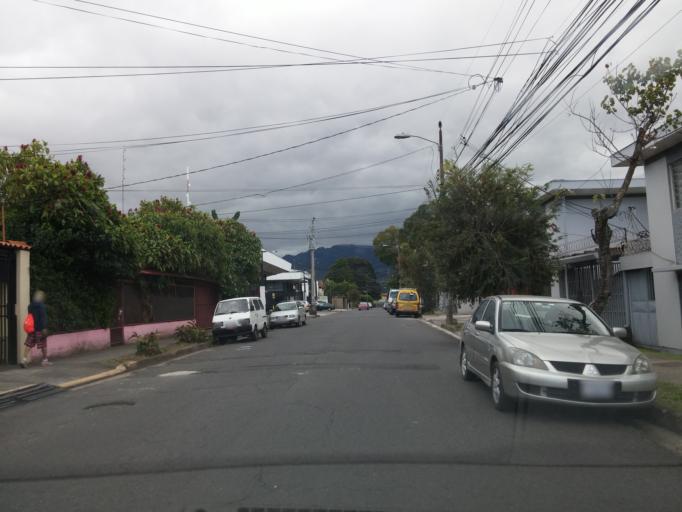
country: CR
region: San Jose
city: San Jose
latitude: 9.9311
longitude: -84.1053
